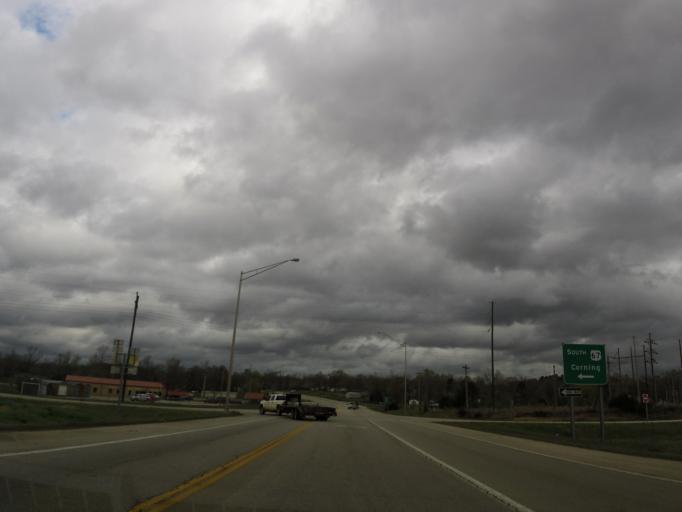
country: US
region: Missouri
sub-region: Butler County
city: Poplar Bluff
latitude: 36.7290
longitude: -90.4628
